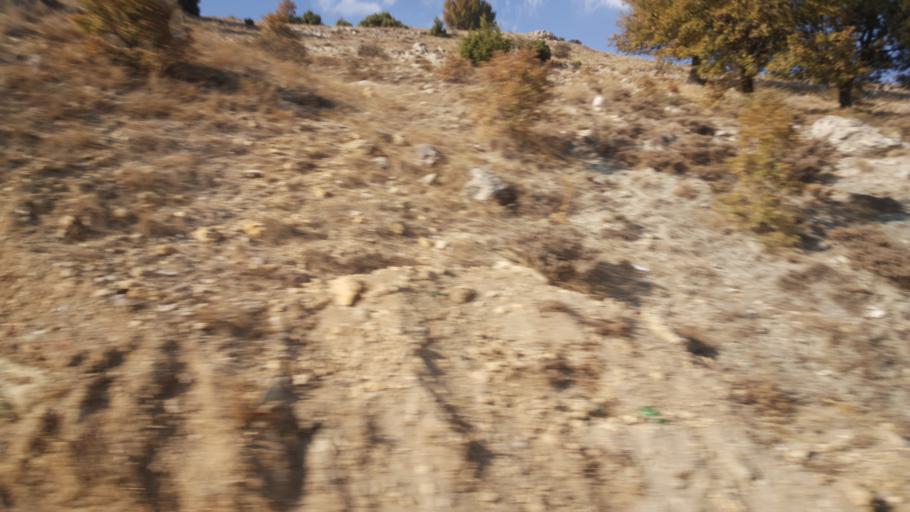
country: TR
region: Eskisehir
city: Kirka
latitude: 39.3248
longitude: 30.5701
